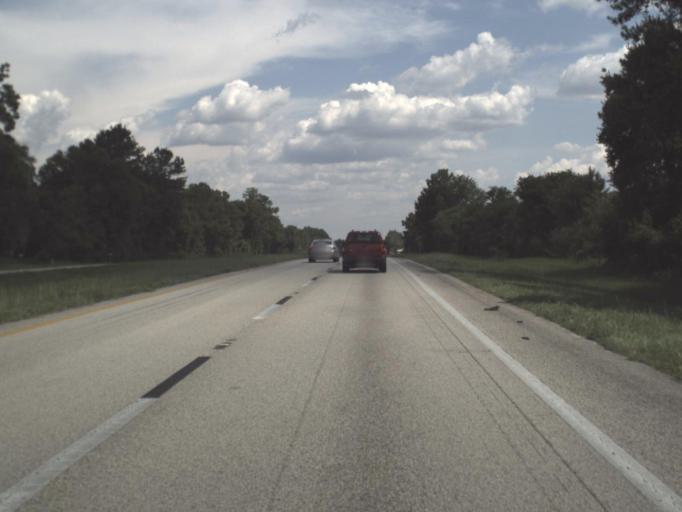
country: US
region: Florida
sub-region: Alachua County
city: Hawthorne
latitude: 29.6680
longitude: -82.1185
